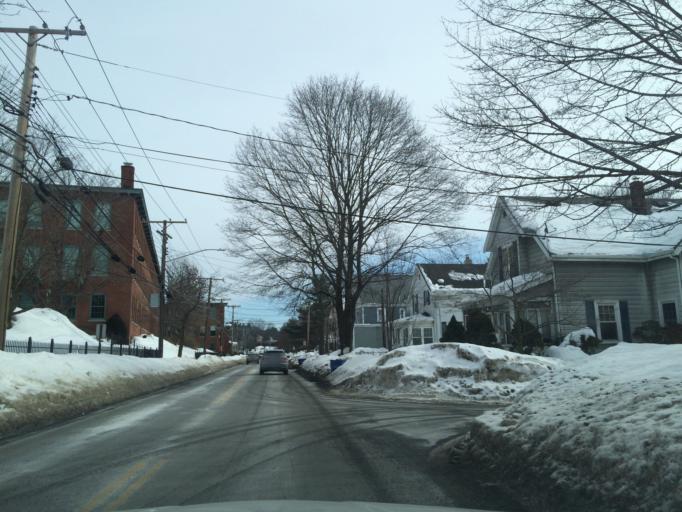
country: US
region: Massachusetts
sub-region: Norfolk County
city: Needham
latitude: 42.3083
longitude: -71.2194
